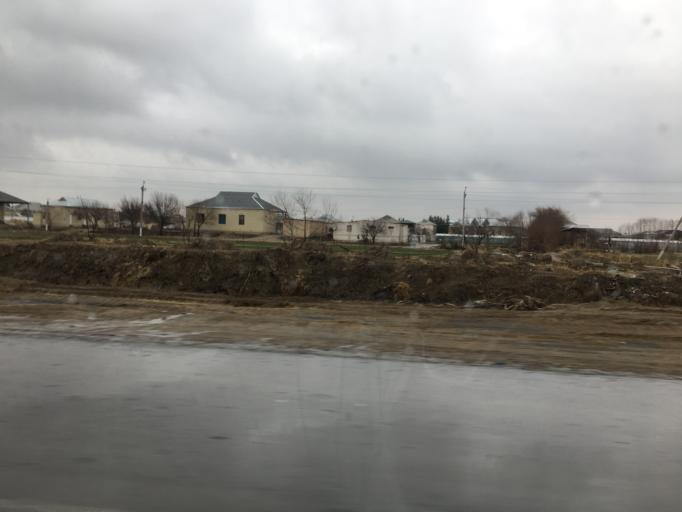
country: TM
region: Mary
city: Mary
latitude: 37.5360
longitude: 61.8849
